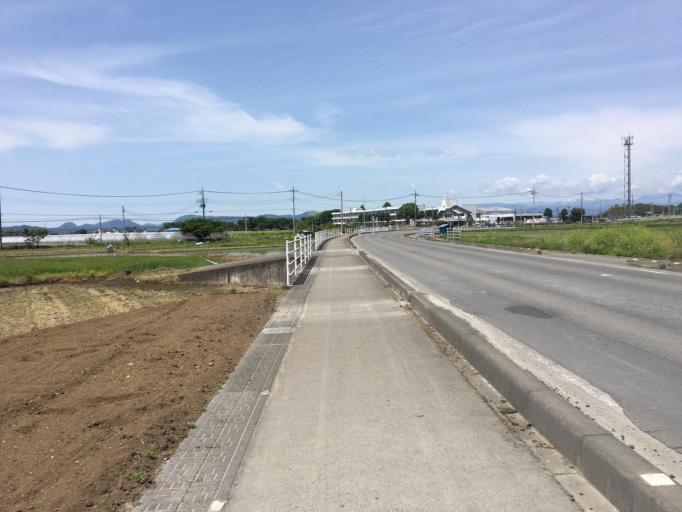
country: JP
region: Tochigi
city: Mibu
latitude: 36.4368
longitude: 139.7997
